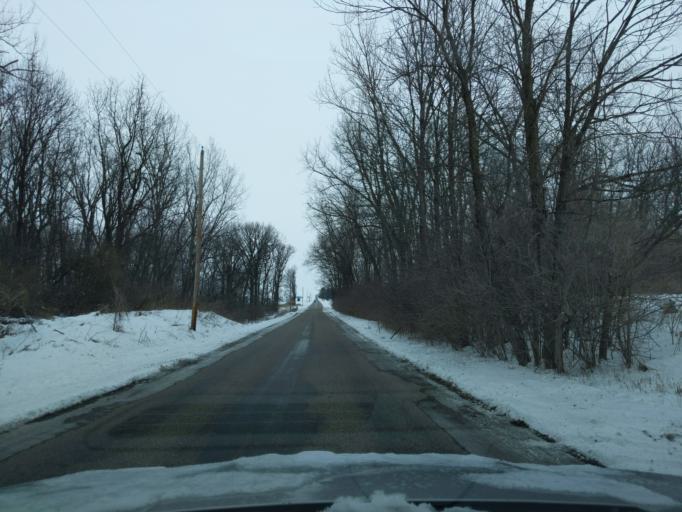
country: US
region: Indiana
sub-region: Benton County
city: Otterbein
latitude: 40.4204
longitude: -87.0918
